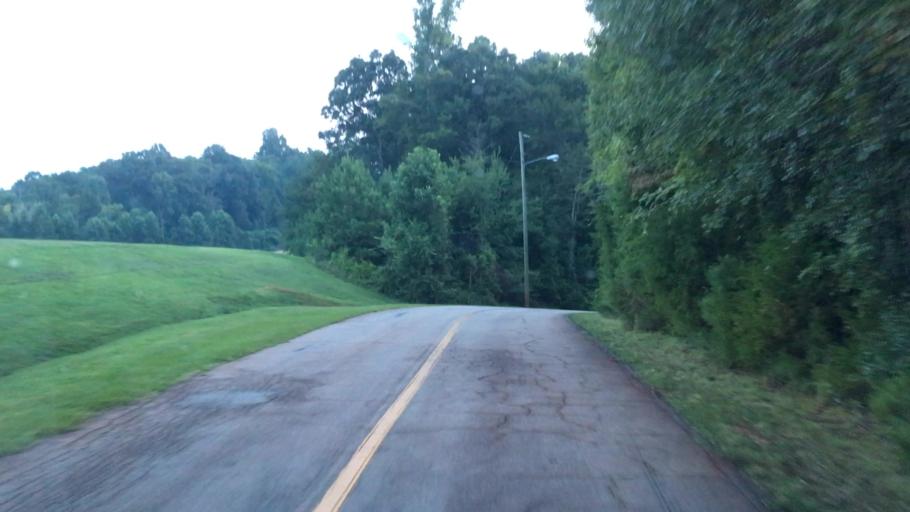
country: US
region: Georgia
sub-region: Jackson County
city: Braselton
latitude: 34.1443
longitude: -83.8142
